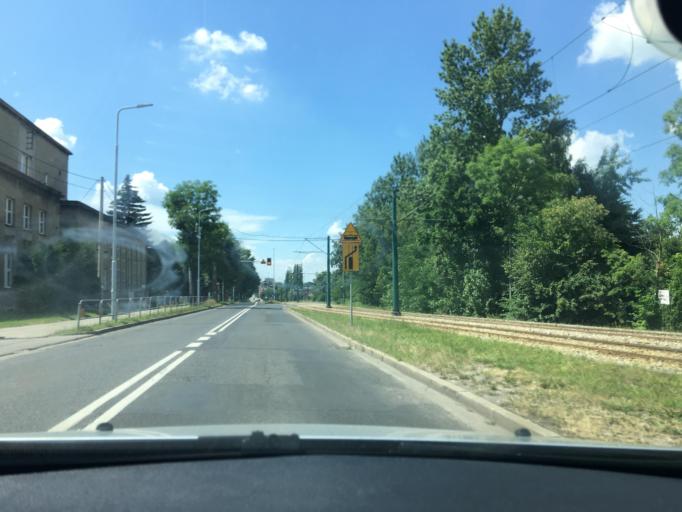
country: PL
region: Silesian Voivodeship
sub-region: Chorzow
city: Chorzow
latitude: 50.2726
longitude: 18.9645
